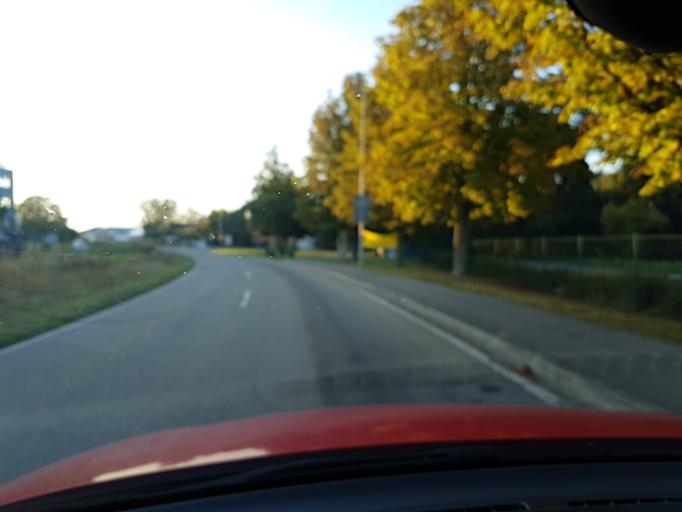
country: DE
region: Baden-Wuerttemberg
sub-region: Regierungsbezirk Stuttgart
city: Eppingen
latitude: 49.1029
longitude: 8.8962
